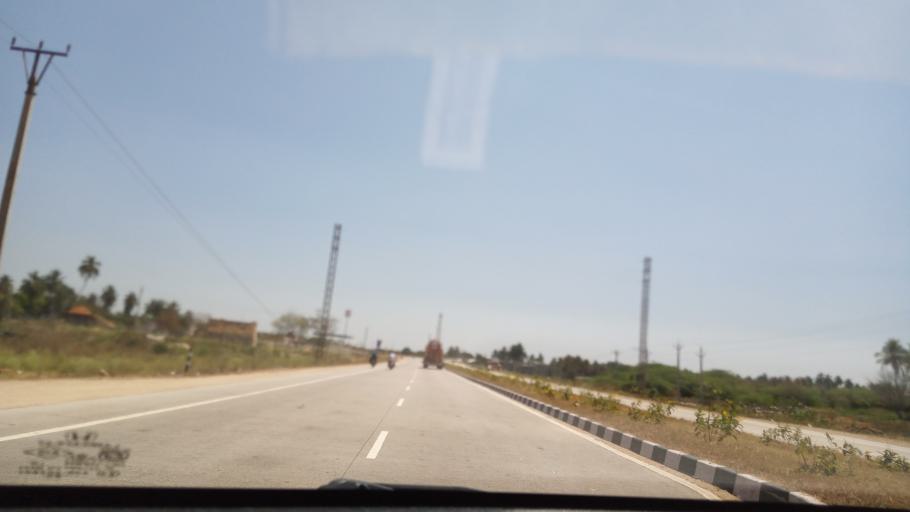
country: IN
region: Andhra Pradesh
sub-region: Chittoor
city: Chittoor
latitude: 13.2020
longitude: 78.9519
